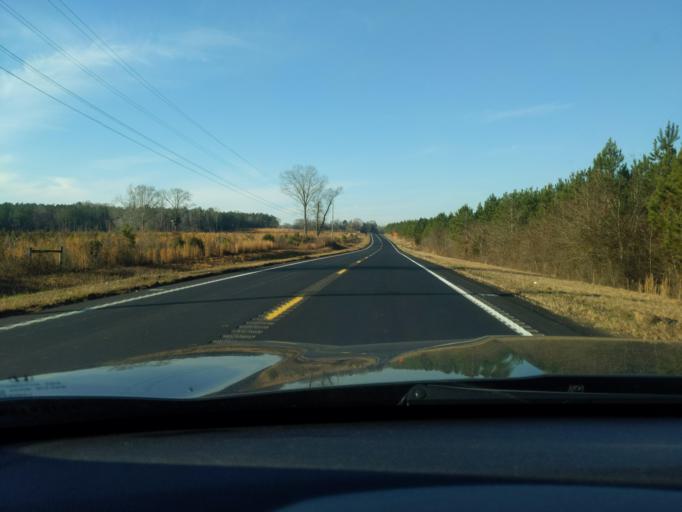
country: US
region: South Carolina
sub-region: Newberry County
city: Newberry
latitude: 34.2075
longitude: -81.7668
